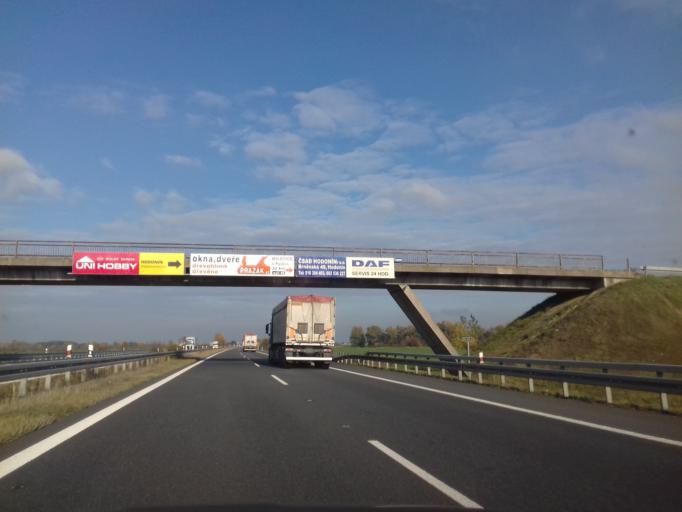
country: CZ
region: South Moravian
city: Kostice
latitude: 48.7646
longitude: 16.9434
